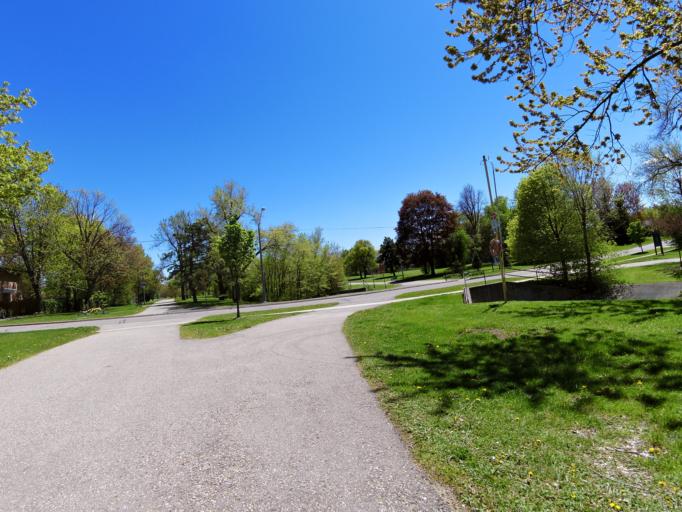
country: CA
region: Ontario
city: Brampton
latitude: 43.7112
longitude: -79.7058
